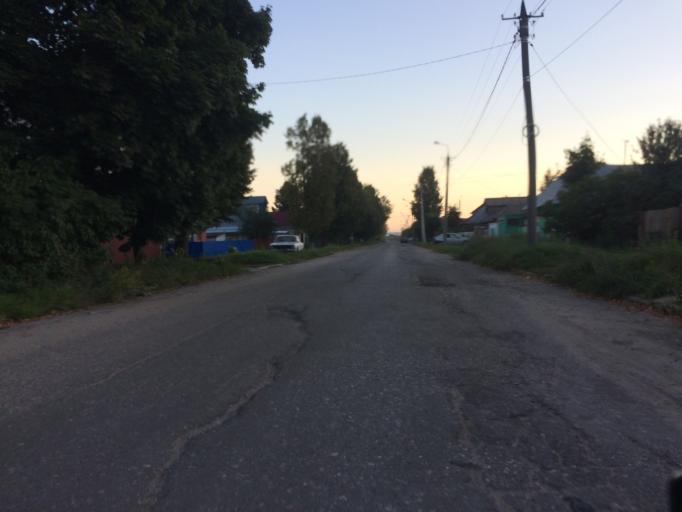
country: RU
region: Mariy-El
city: Yoshkar-Ola
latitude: 56.6515
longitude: 47.9034
